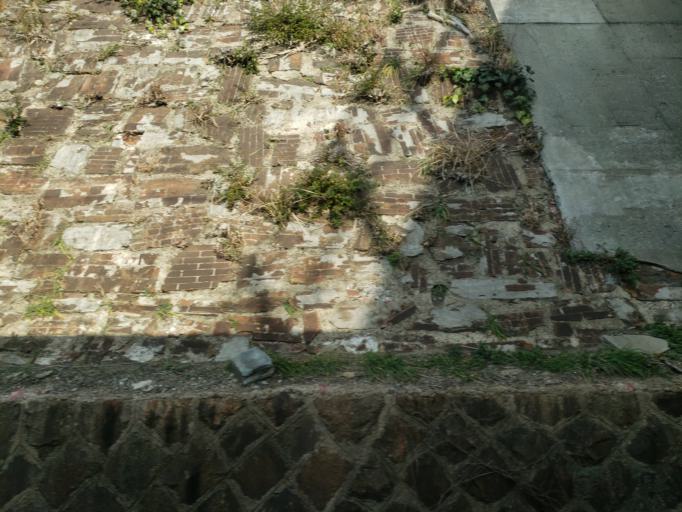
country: JP
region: Hyogo
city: Ashiya
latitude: 34.7331
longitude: 135.3017
